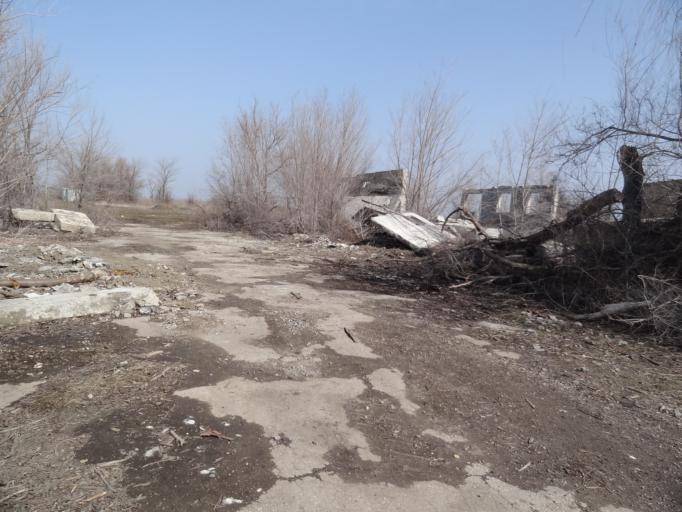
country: RU
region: Saratov
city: Shumeyka
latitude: 51.4358
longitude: 46.2262
